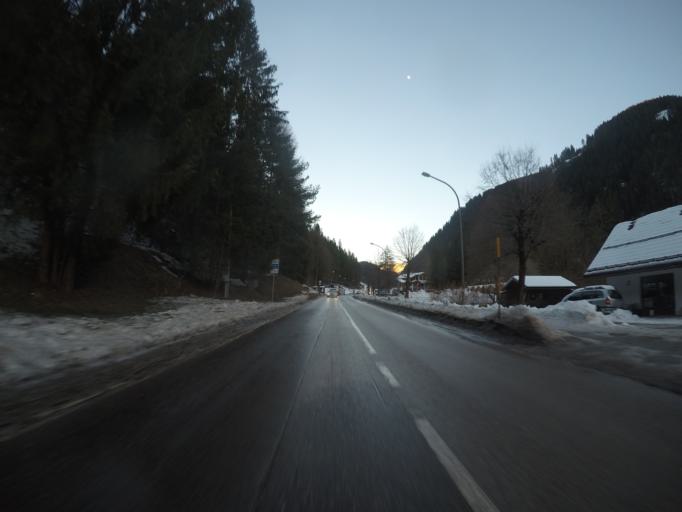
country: IT
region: Trentino-Alto Adige
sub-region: Provincia di Trento
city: Predazzo
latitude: 46.3115
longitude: 11.6152
